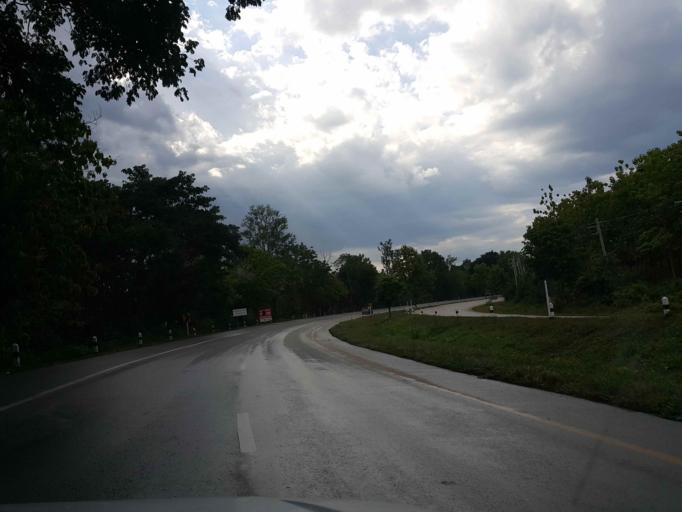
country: TH
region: Lampang
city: Thoen
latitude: 17.6615
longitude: 99.2461
